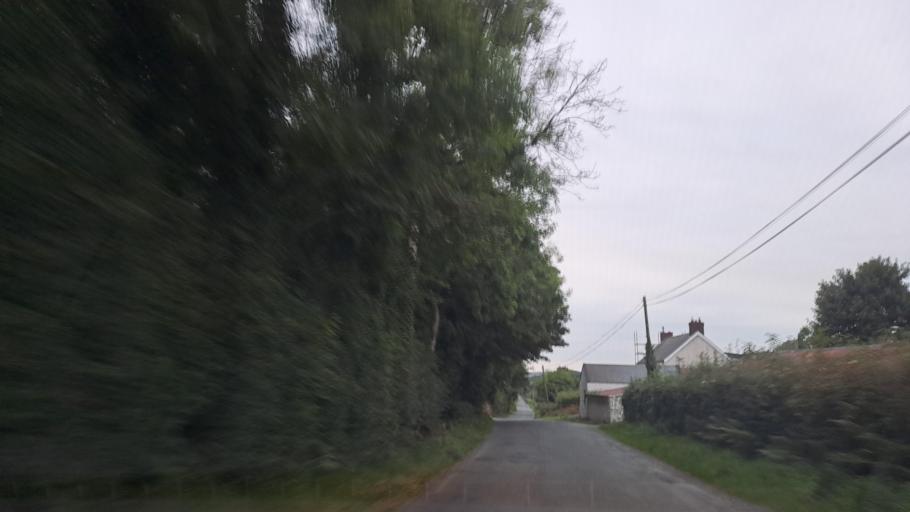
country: IE
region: Ulster
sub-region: County Monaghan
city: Carrickmacross
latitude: 54.0325
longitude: -6.8095
